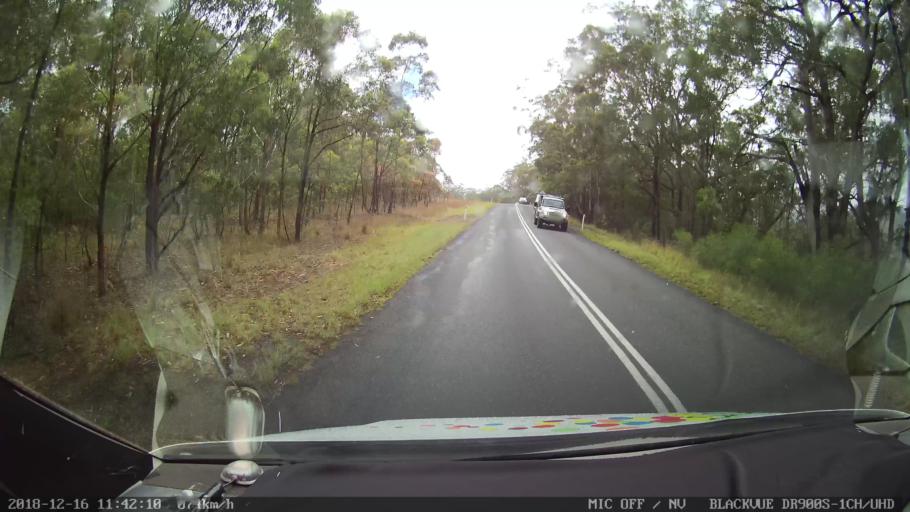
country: AU
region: New South Wales
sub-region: Tenterfield Municipality
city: Carrolls Creek
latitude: -28.9544
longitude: 152.2148
